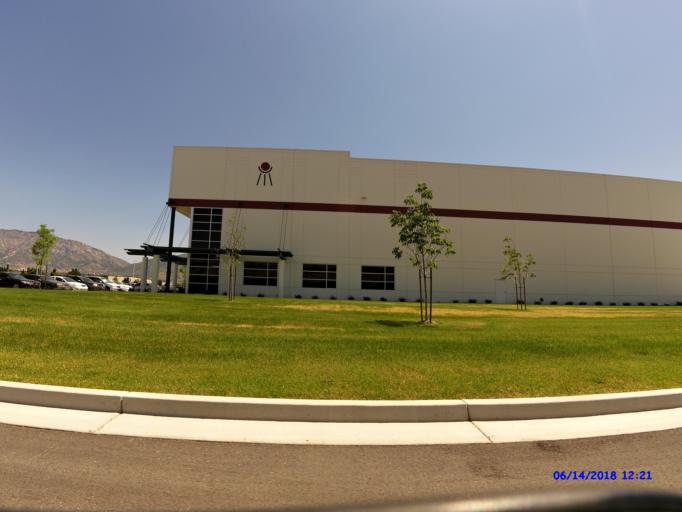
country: US
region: Utah
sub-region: Weber County
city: Harrisville
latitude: 41.2661
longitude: -112.0046
